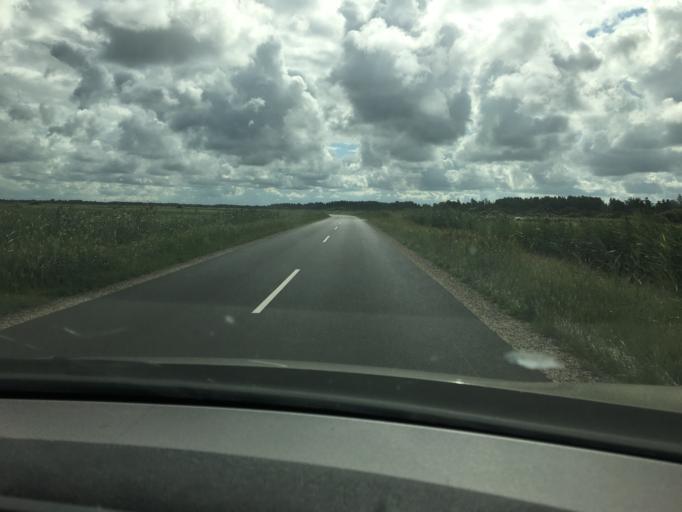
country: DK
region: Central Jutland
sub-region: Ringkobing-Skjern Kommune
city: Hvide Sande
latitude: 55.8288
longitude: 8.2306
